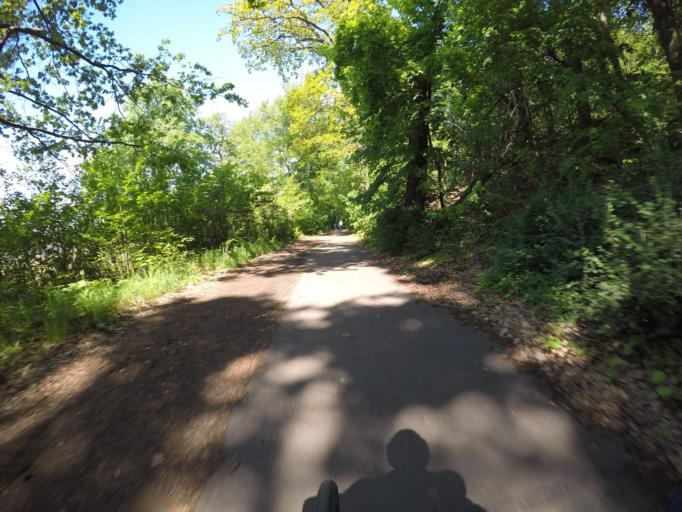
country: DE
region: Berlin
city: Wannsee
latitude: 52.4268
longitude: 13.1194
